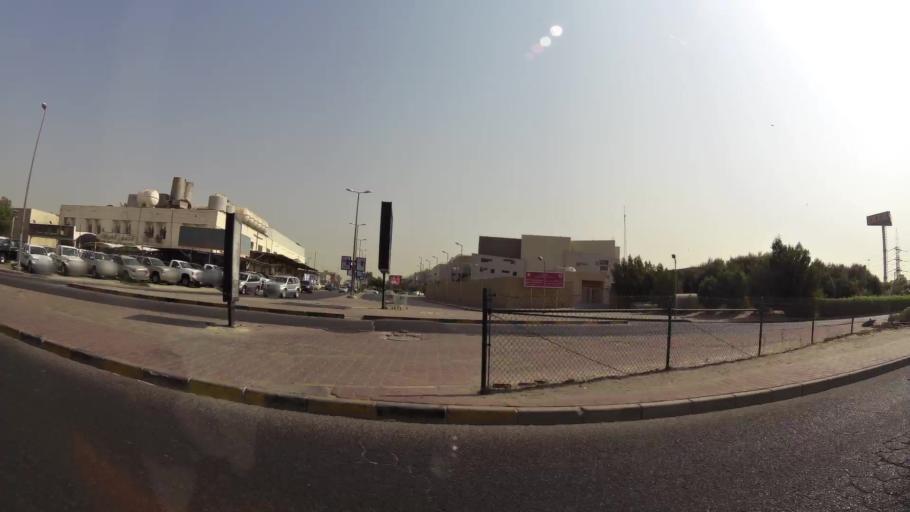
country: KW
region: Al Asimah
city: Ar Rabiyah
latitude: 29.3031
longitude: 47.9274
